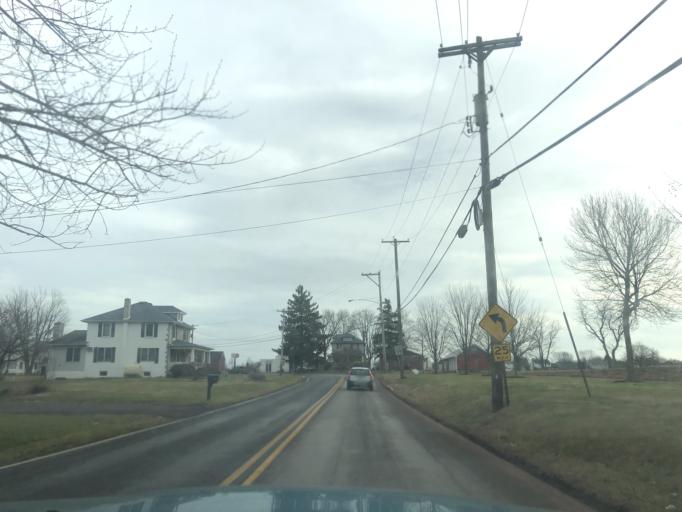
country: US
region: Pennsylvania
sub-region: Montgomery County
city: Harleysville
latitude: 40.2774
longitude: -75.4007
